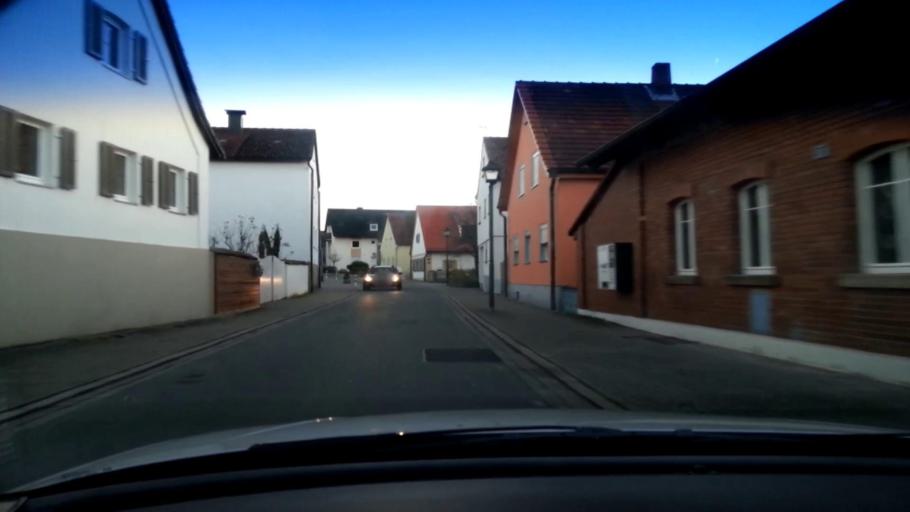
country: DE
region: Bavaria
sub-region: Upper Franconia
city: Memmelsdorf
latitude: 49.9311
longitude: 10.9541
